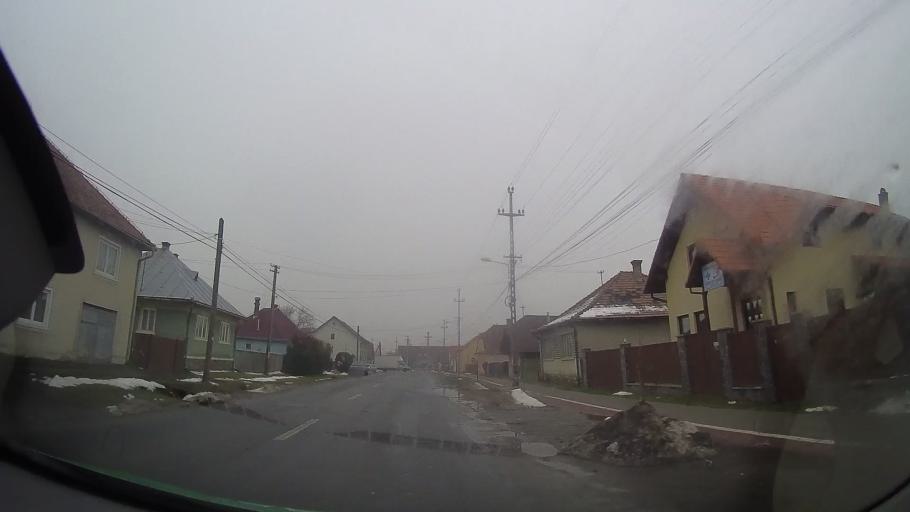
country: RO
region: Harghita
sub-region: Municipiul Gheorgheni
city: Gheorgheni
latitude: 46.7262
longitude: 25.6140
